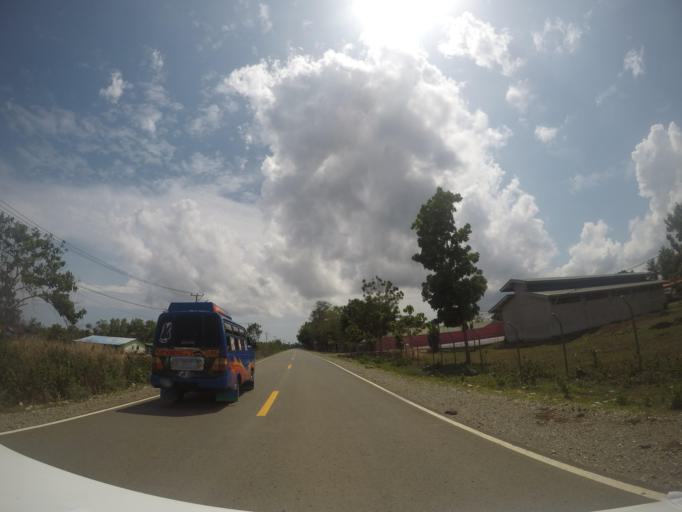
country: TL
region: Baucau
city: Baucau
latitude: -8.4775
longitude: 126.3988
